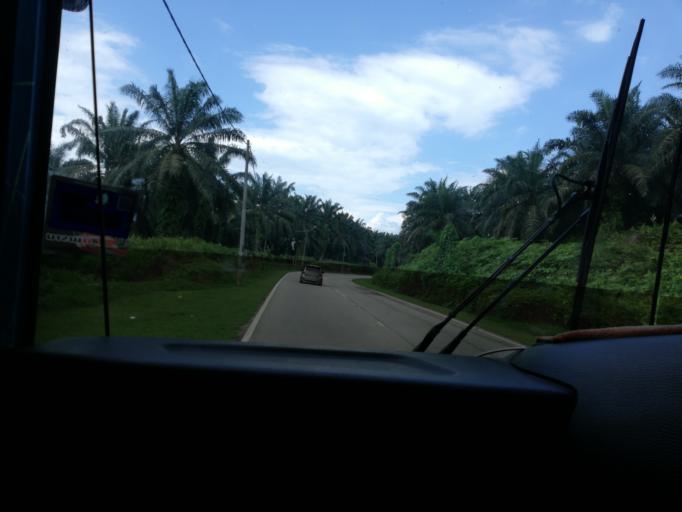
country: MY
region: Kedah
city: Kulim
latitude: 5.2666
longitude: 100.6095
